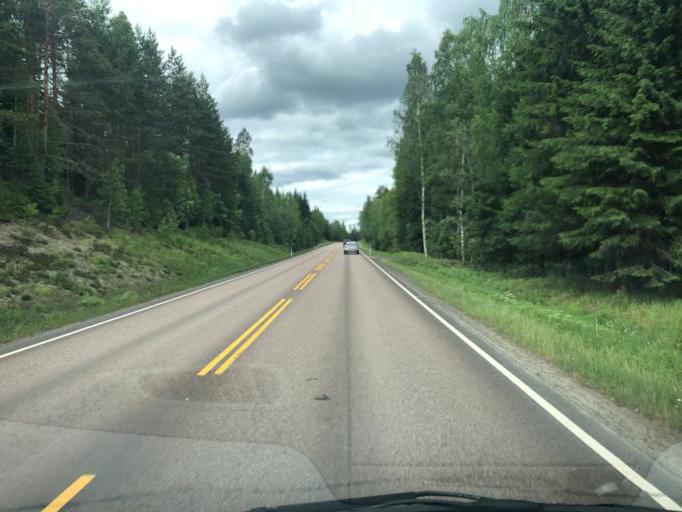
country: FI
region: Kymenlaakso
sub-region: Kouvola
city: Kouvola
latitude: 61.0319
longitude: 26.9862
